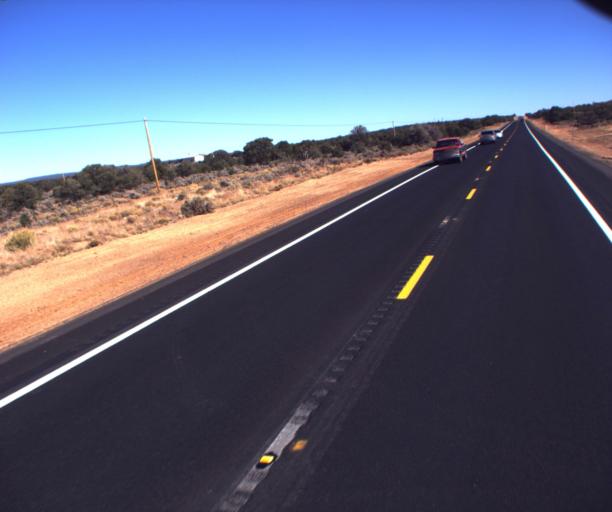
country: US
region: Arizona
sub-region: Apache County
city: Ganado
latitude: 35.7179
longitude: -109.3974
